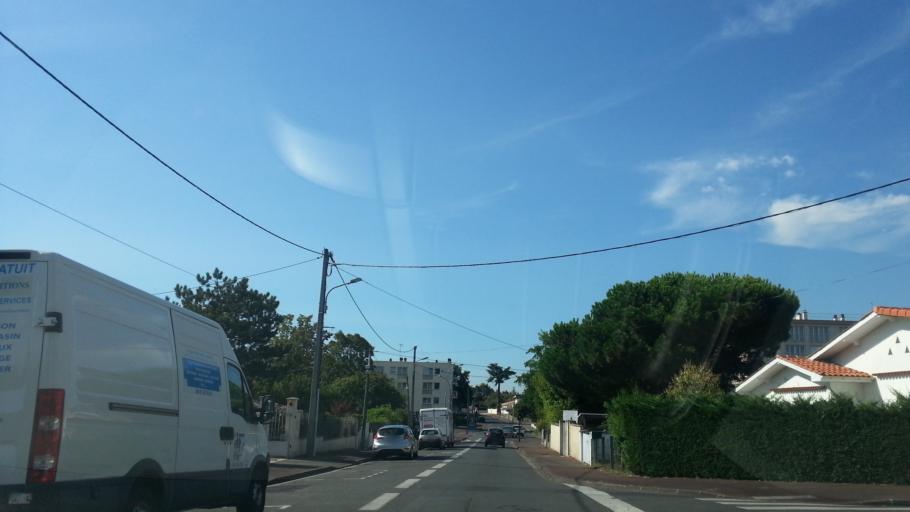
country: FR
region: Aquitaine
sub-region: Departement de la Gironde
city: Villenave-d'Ornon
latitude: 44.7652
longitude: -0.5655
